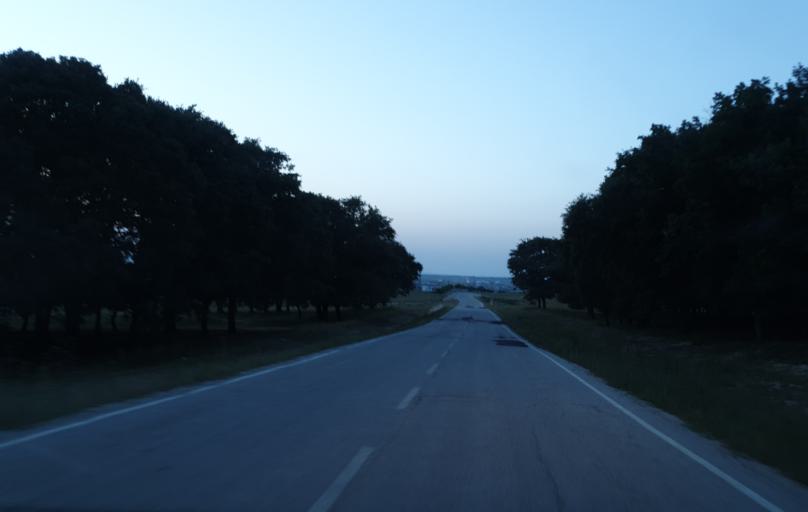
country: TR
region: Tekirdag
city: Saray
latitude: 41.3567
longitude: 27.9276
